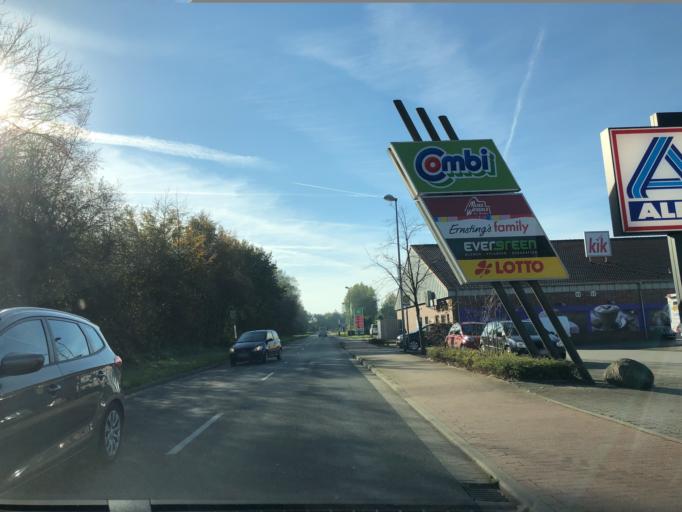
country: DE
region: Lower Saxony
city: Lehe
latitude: 53.0486
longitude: 7.3270
